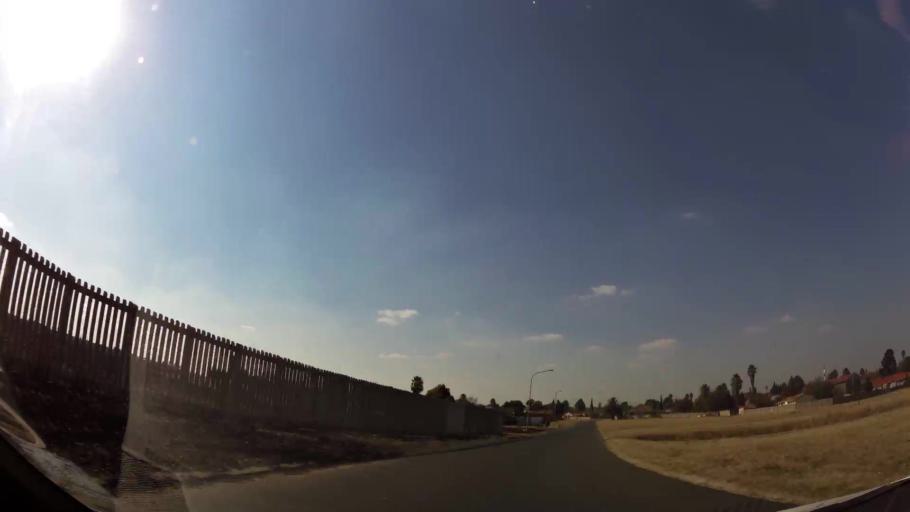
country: ZA
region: Gauteng
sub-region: Ekurhuleni Metropolitan Municipality
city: Benoni
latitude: -26.2403
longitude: 28.3075
